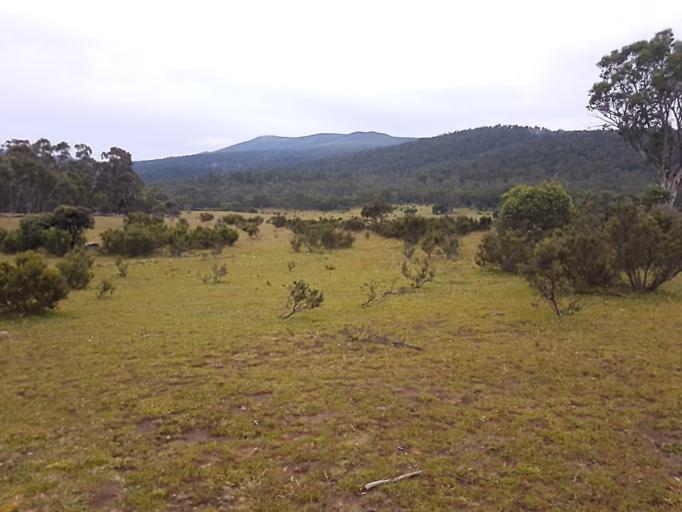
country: AU
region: New South Wales
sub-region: Snowy River
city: Jindabyne
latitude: -36.7968
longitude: 148.1683
